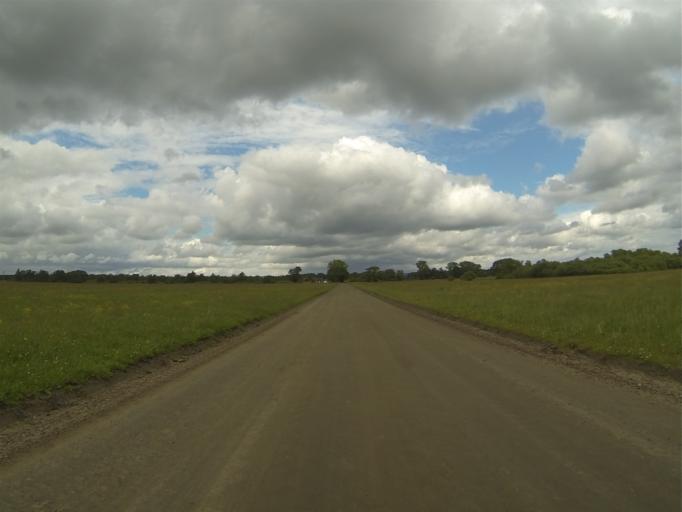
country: SE
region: Skane
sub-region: Lunds Kommun
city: Veberod
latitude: 55.6998
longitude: 13.4277
